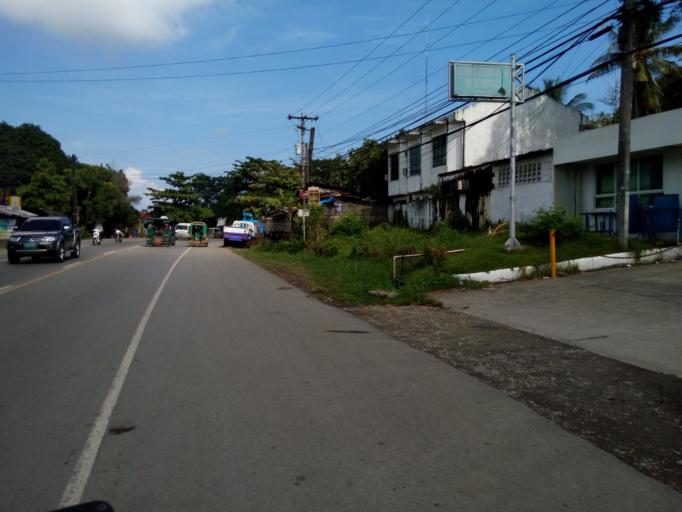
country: PH
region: Caraga
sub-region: Province of Surigao del Norte
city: Surigao
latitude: 9.7769
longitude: 125.4823
